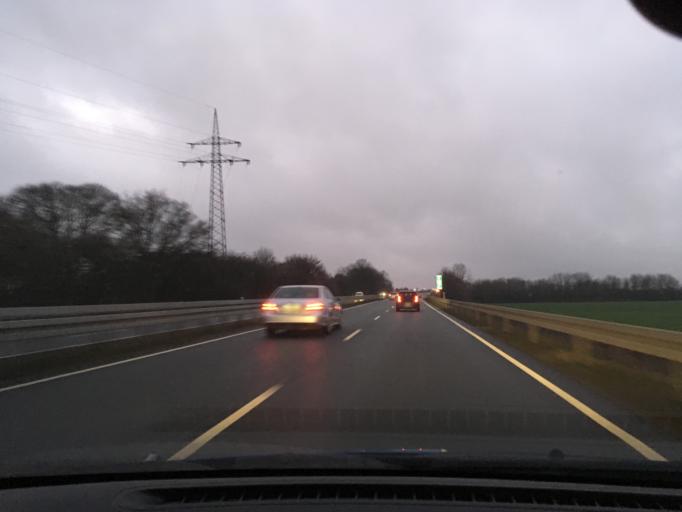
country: DE
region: Lower Saxony
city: Lehrte
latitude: 52.3588
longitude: 9.8936
